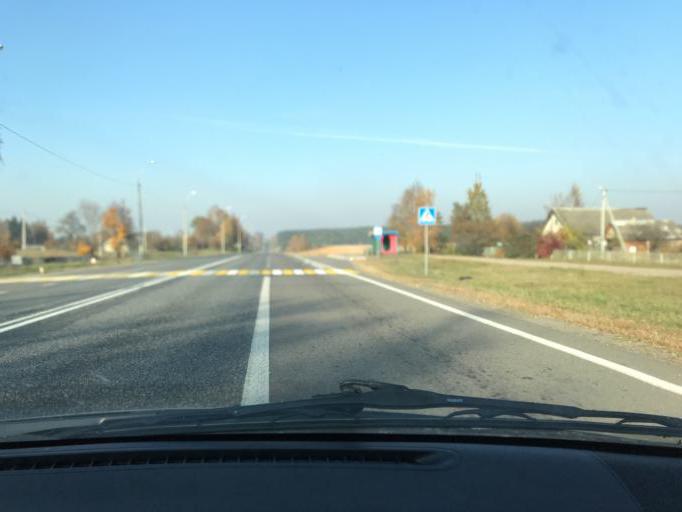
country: BY
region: Vitebsk
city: Orsha
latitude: 54.3778
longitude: 30.4441
